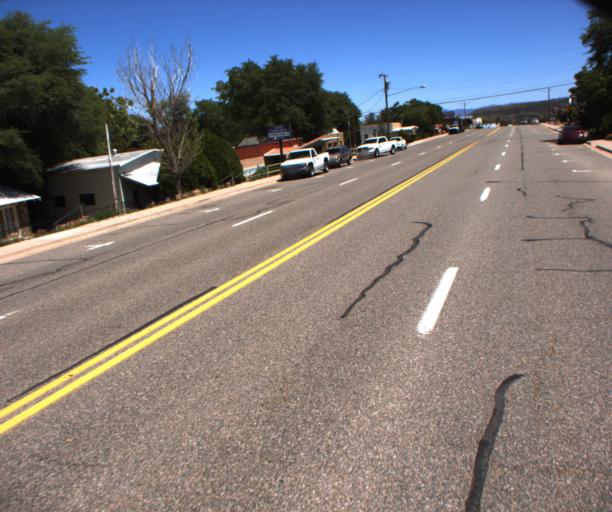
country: US
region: Arizona
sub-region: Yavapai County
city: Congress
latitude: 34.2211
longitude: -112.7477
